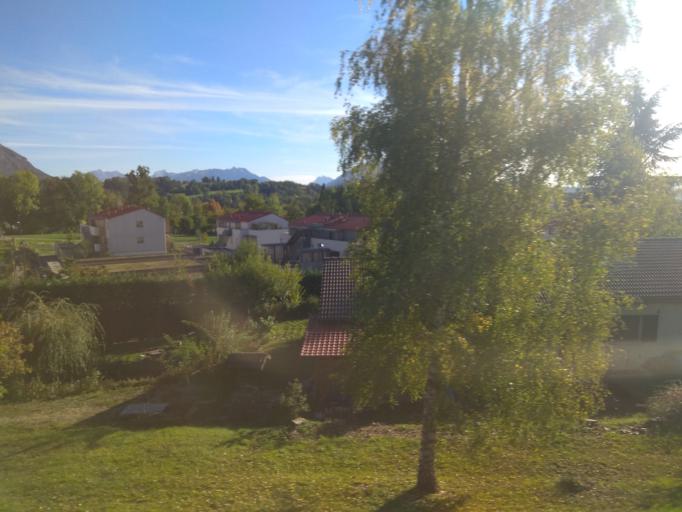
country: FR
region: Rhone-Alpes
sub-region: Departement de la Haute-Savoie
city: Pringy
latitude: 45.9426
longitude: 6.1410
